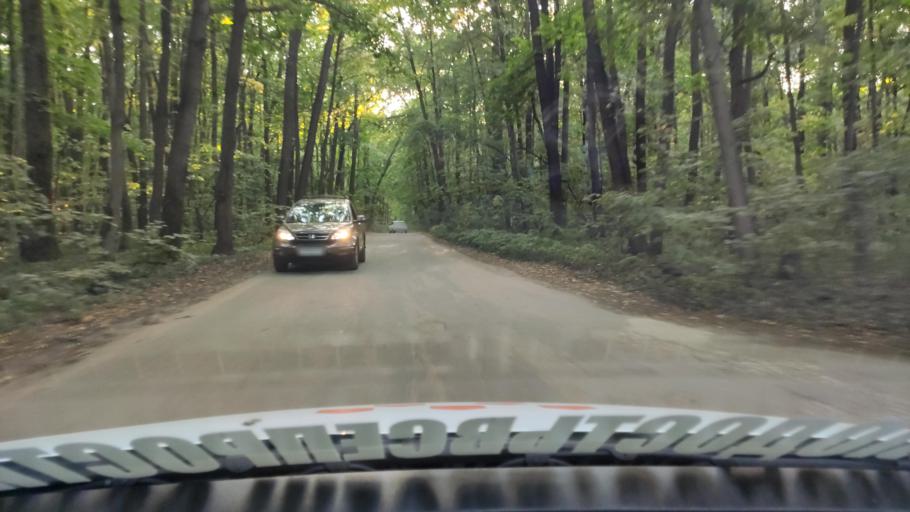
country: RU
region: Voronezj
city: Podgornoye
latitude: 51.7433
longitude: 39.2194
